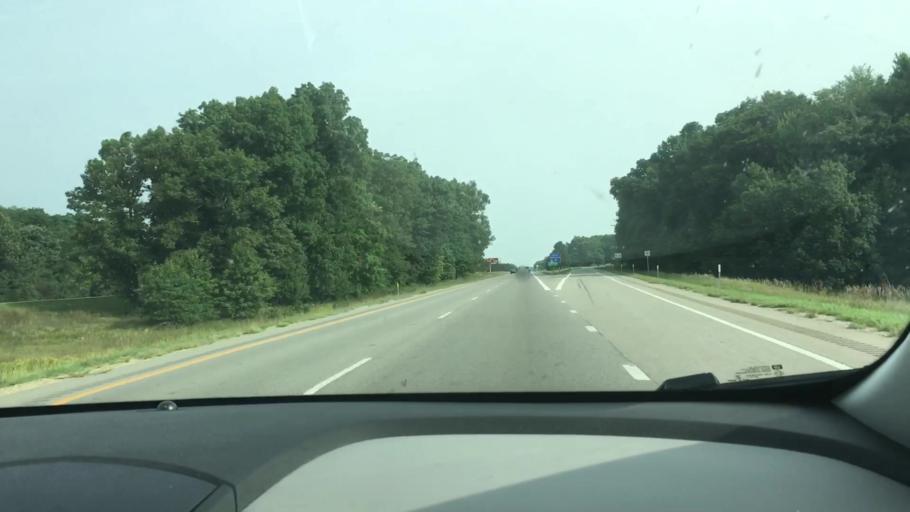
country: US
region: Michigan
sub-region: Kalamazoo County
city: Schoolcraft
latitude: 42.1685
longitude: -85.6446
